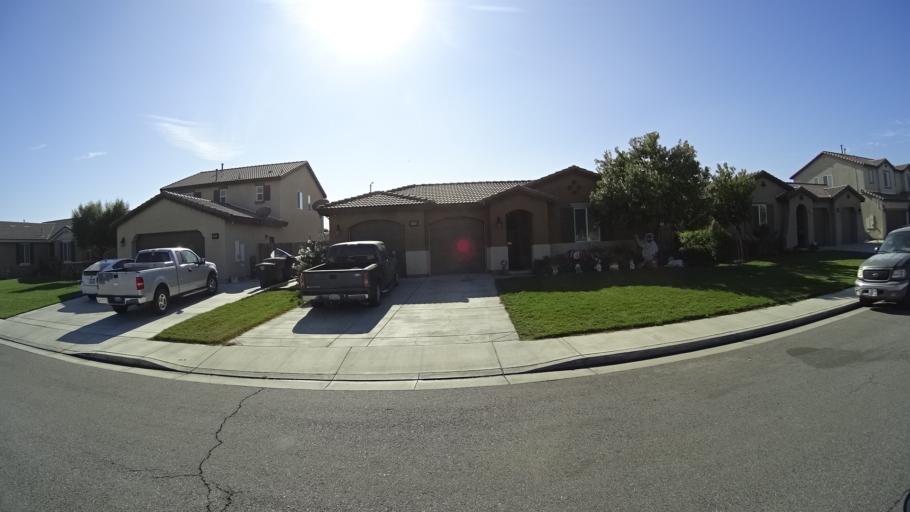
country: US
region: California
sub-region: Kern County
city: Greenfield
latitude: 35.2748
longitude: -119.0674
